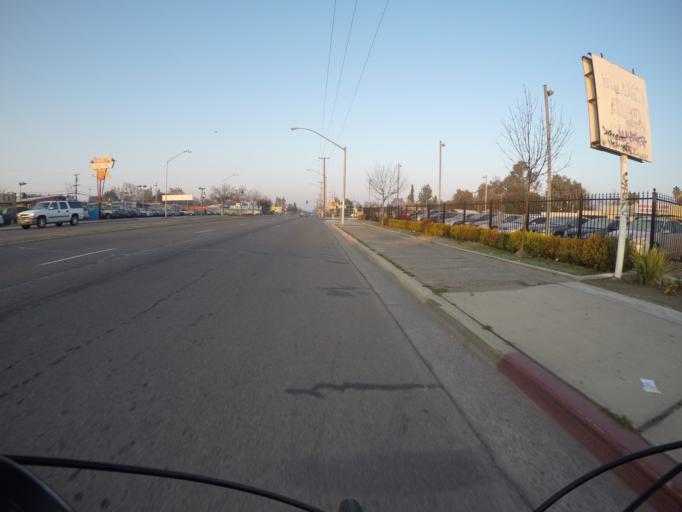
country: US
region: California
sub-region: Fresno County
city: Fresno
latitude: 36.7506
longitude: -119.7662
